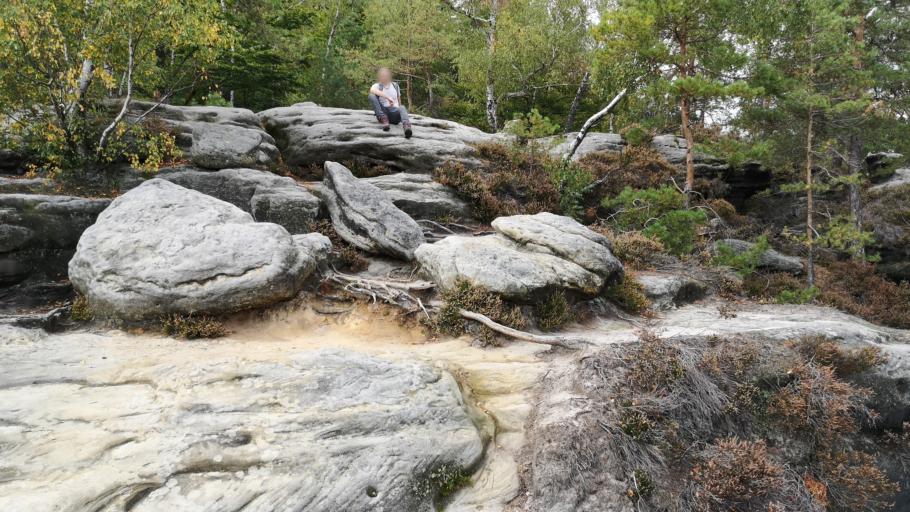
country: DE
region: Saxony
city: Sebnitz
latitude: 50.9126
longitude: 14.2607
